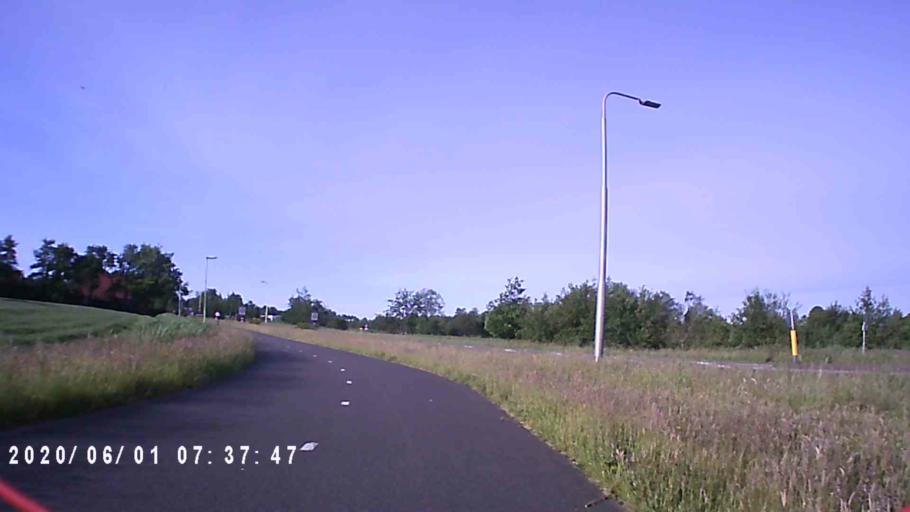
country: NL
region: Friesland
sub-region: Gemeente Dantumadiel
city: Damwald
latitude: 53.2975
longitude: 5.9964
